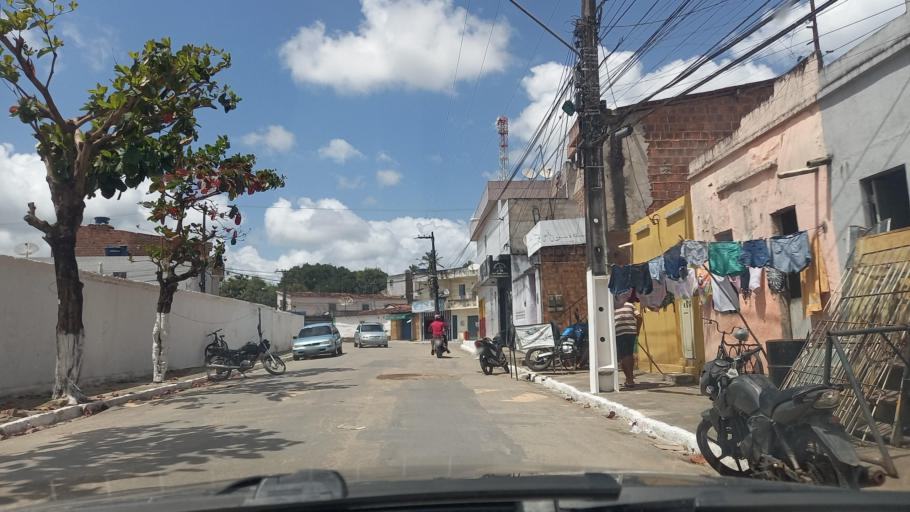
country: BR
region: Pernambuco
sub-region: Goiana
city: Goiana
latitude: -7.5608
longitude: -35.0090
